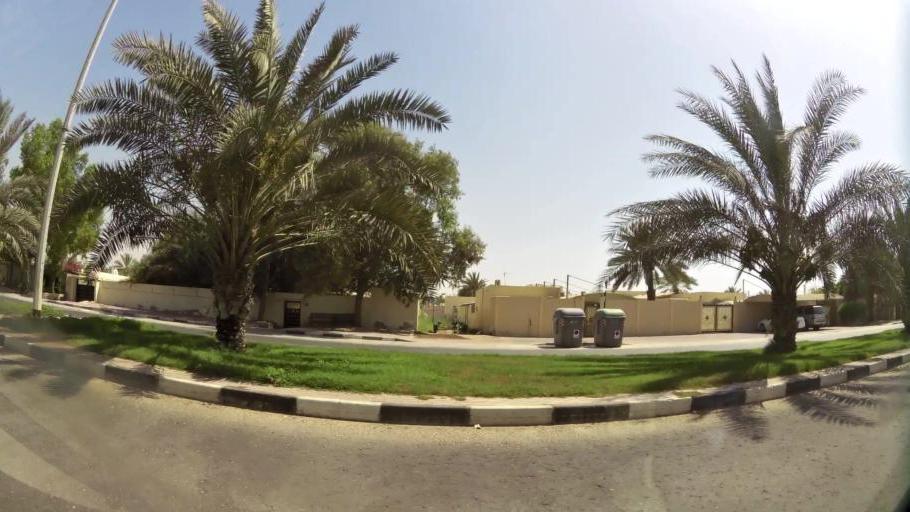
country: AE
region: Ajman
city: Ajman
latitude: 25.4137
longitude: 55.4751
